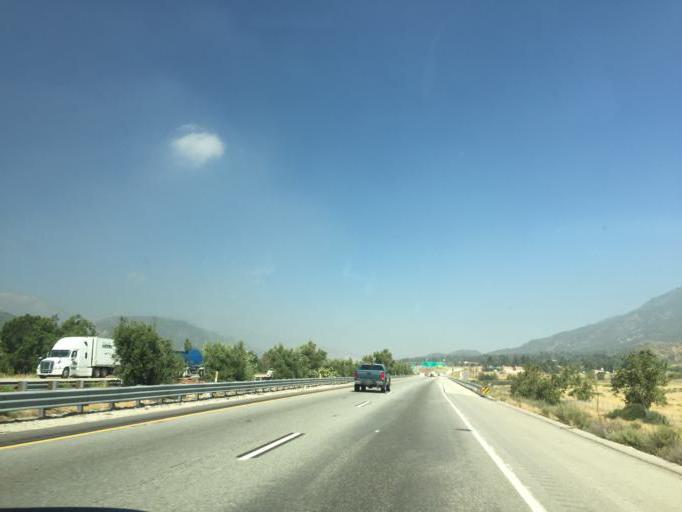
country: US
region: California
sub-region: San Bernardino County
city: Muscoy
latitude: 34.2162
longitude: -117.3938
